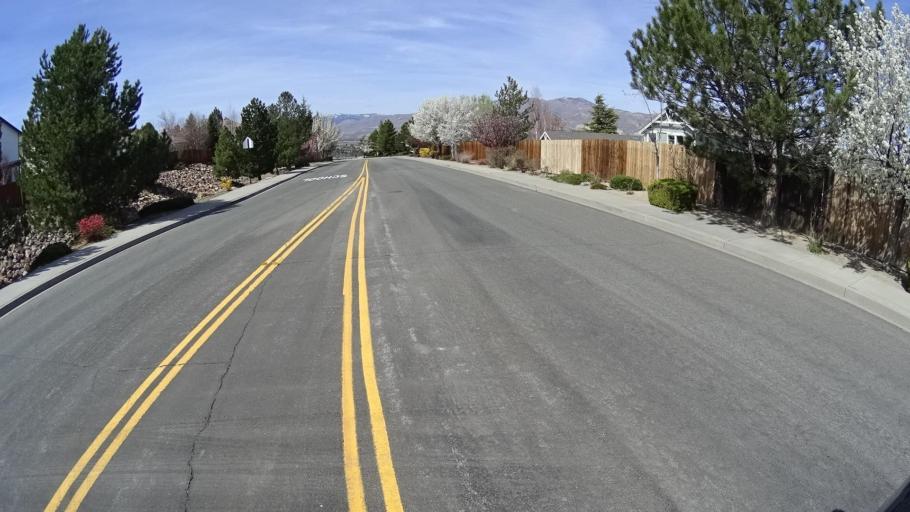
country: US
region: Nevada
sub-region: Washoe County
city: Reno
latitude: 39.4848
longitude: -119.8581
